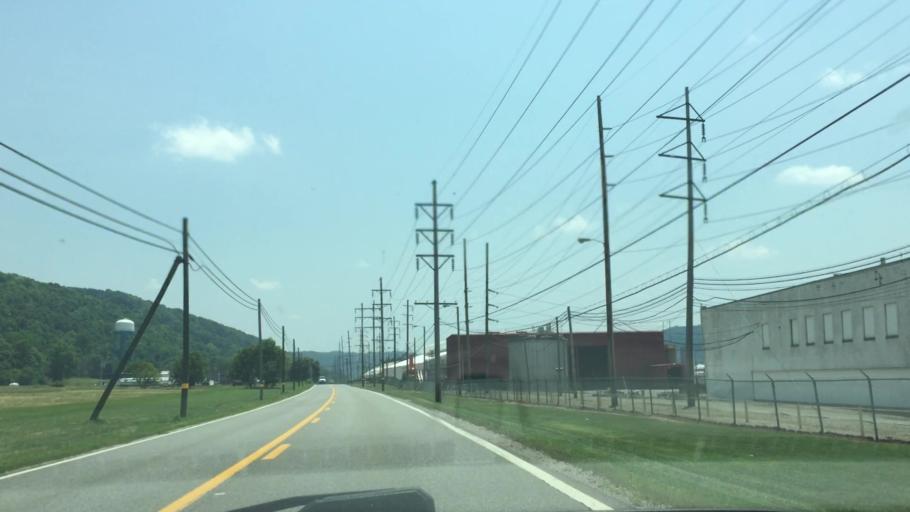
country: US
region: West Virginia
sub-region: Wetzel County
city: New Martinsville
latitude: 39.7530
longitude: -80.8549
